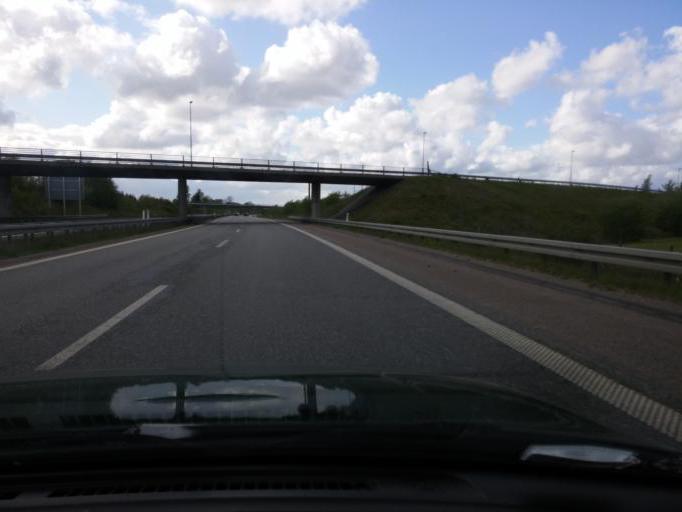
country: DK
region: South Denmark
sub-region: Faaborg-Midtfyn Kommune
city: Ringe
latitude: 55.2439
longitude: 10.4851
